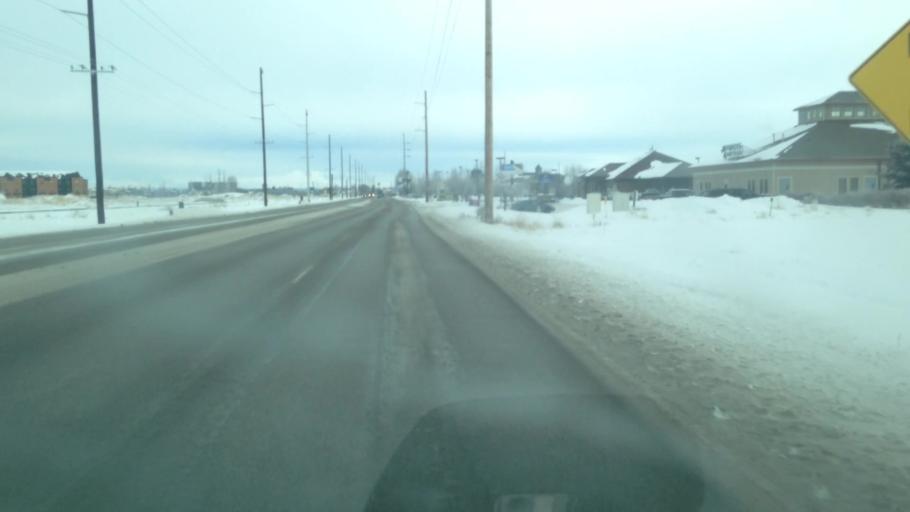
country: US
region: Idaho
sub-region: Madison County
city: Rexburg
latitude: 43.8060
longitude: -111.8071
